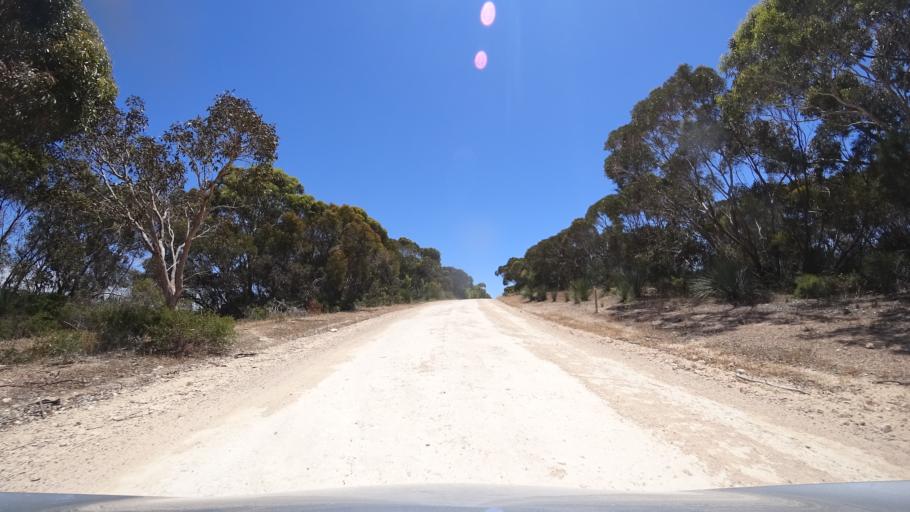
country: AU
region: South Australia
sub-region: Kangaroo Island
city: Kingscote
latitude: -35.6735
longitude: 137.1270
